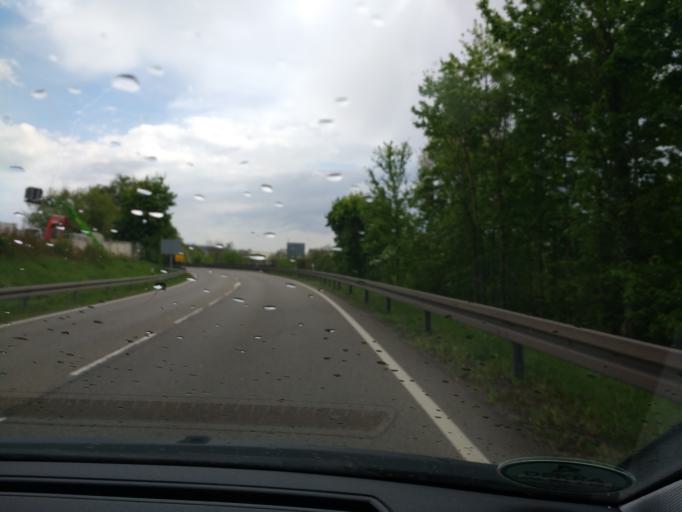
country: FR
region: Lorraine
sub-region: Departement de la Moselle
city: Alsting
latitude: 49.2040
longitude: 7.0206
